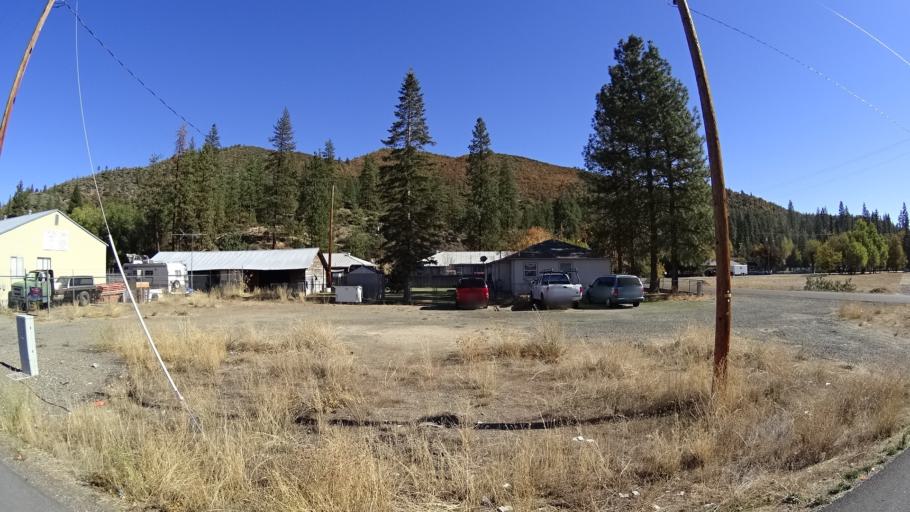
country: US
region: California
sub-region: Siskiyou County
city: Yreka
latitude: 41.6129
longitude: -122.8392
